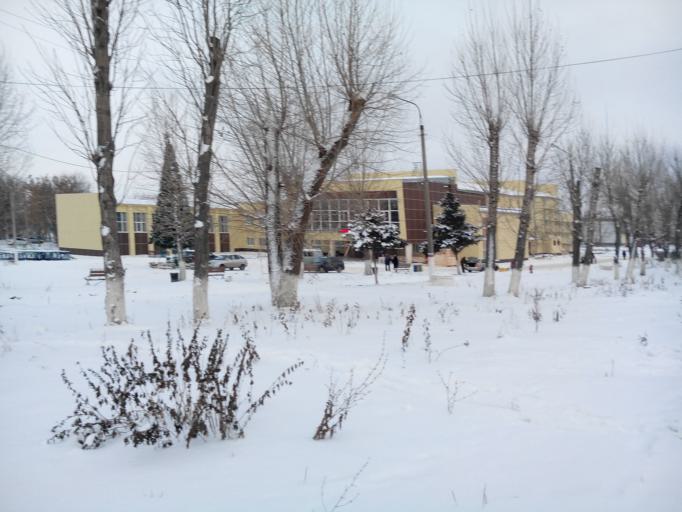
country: RU
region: Tula
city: Yefremov
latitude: 53.1480
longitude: 38.0854
